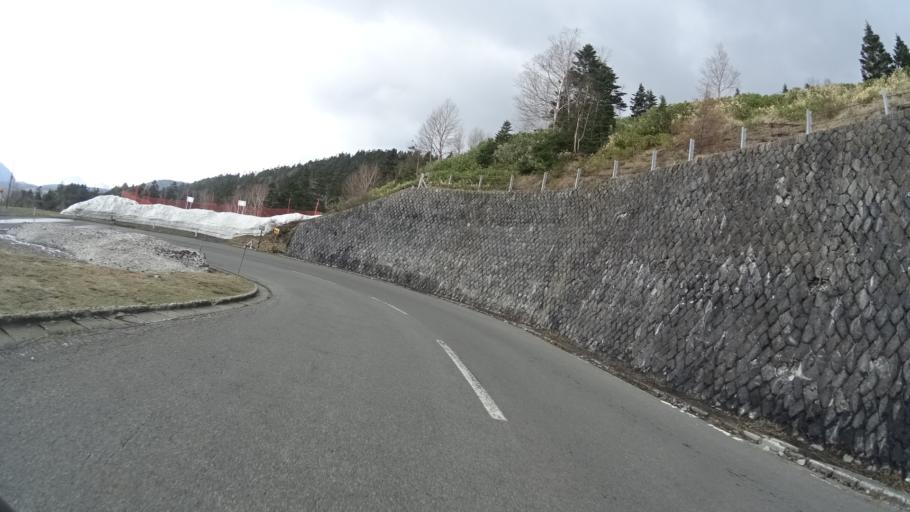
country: JP
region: Nagano
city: Nakano
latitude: 36.6706
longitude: 138.5190
